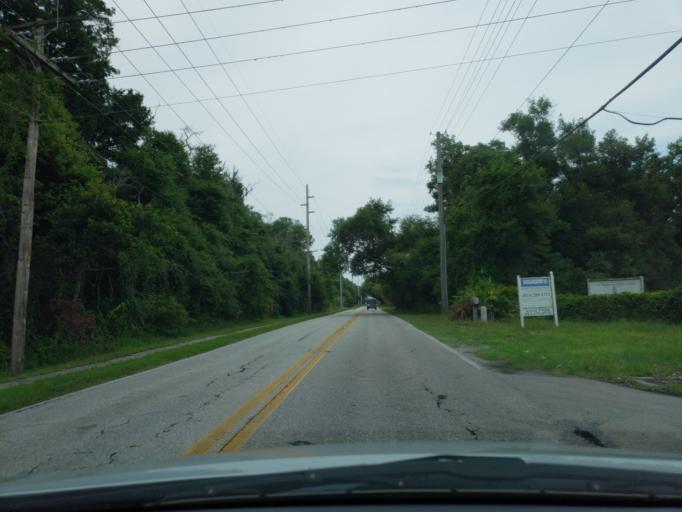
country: US
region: Florida
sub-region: Hillsborough County
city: Lutz
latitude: 28.1424
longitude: -82.4604
